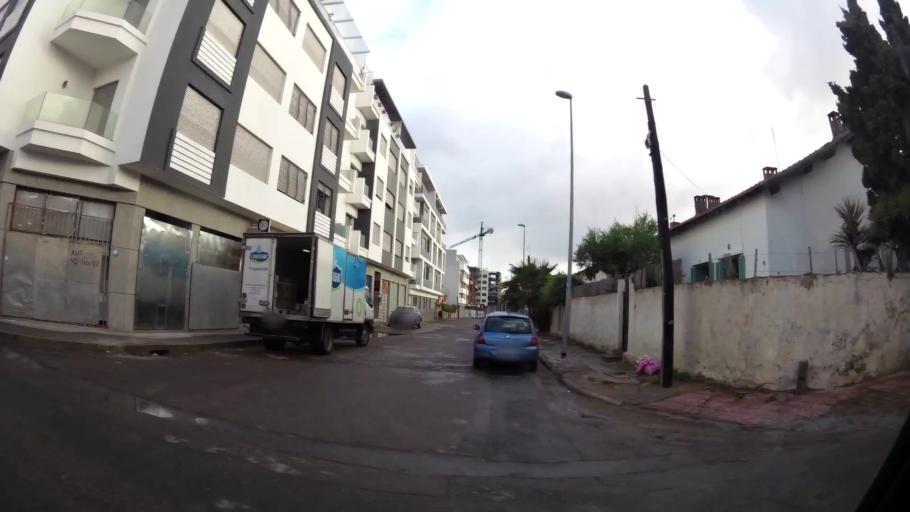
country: MA
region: Grand Casablanca
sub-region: Casablanca
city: Casablanca
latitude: 33.5630
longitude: -7.6475
